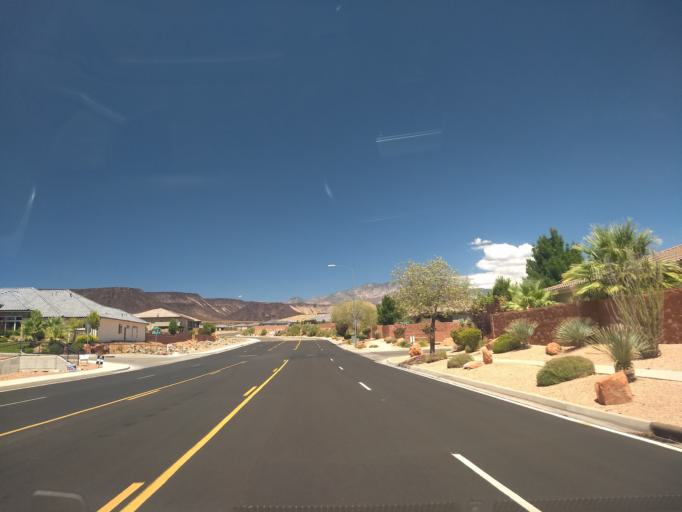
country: US
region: Utah
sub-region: Washington County
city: Washington
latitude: 37.1554
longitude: -113.5258
